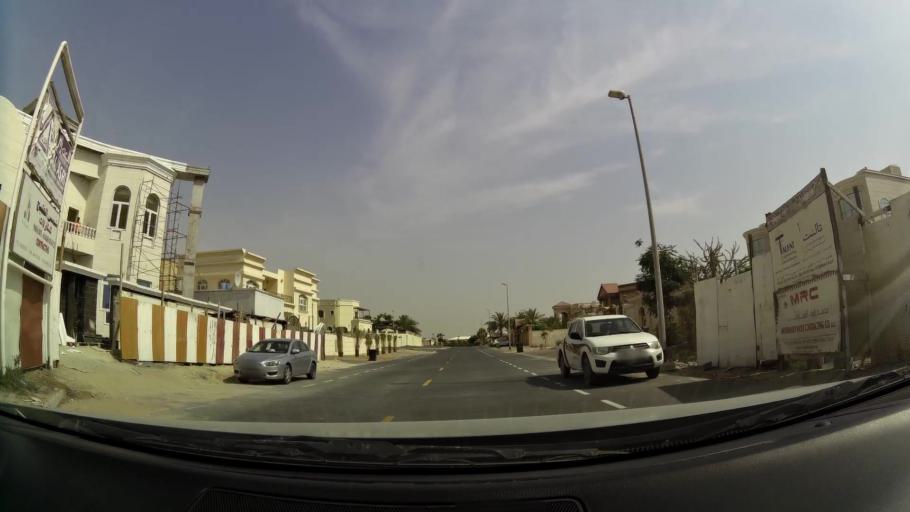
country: AE
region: Ash Shariqah
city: Sharjah
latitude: 25.2540
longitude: 55.4356
